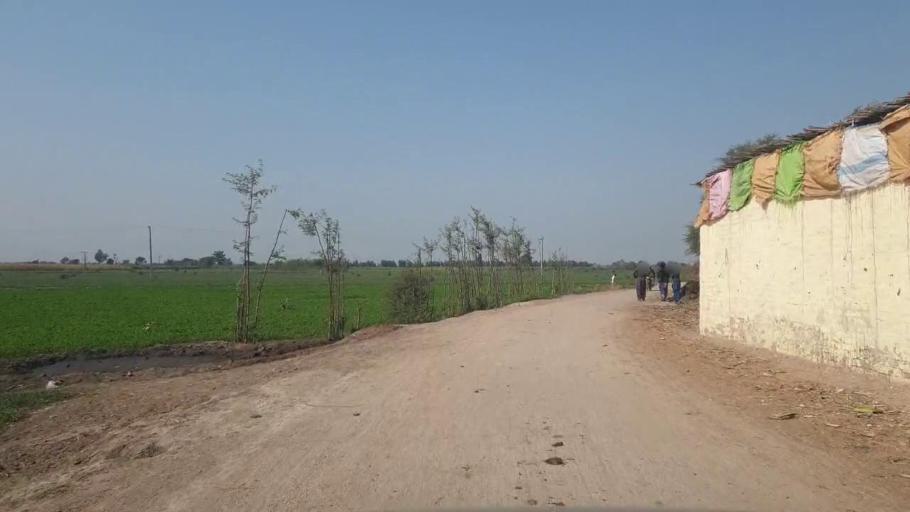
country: PK
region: Sindh
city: Tando Adam
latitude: 25.7891
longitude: 68.6326
